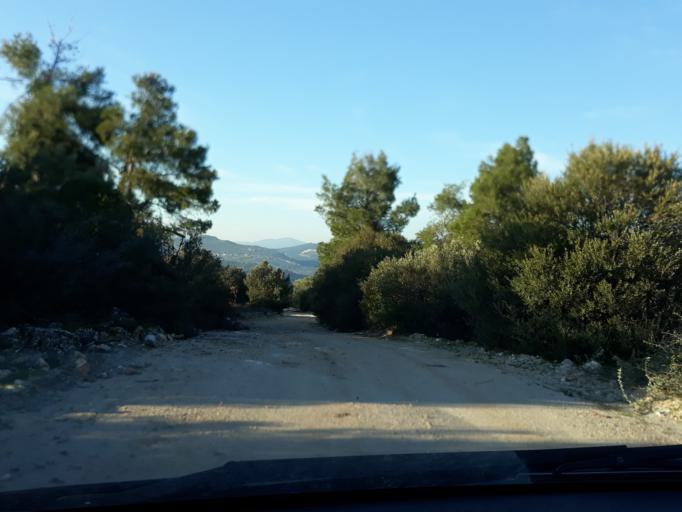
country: GR
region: Central Greece
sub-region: Nomos Voiotias
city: Asopia
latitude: 38.2697
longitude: 23.5291
